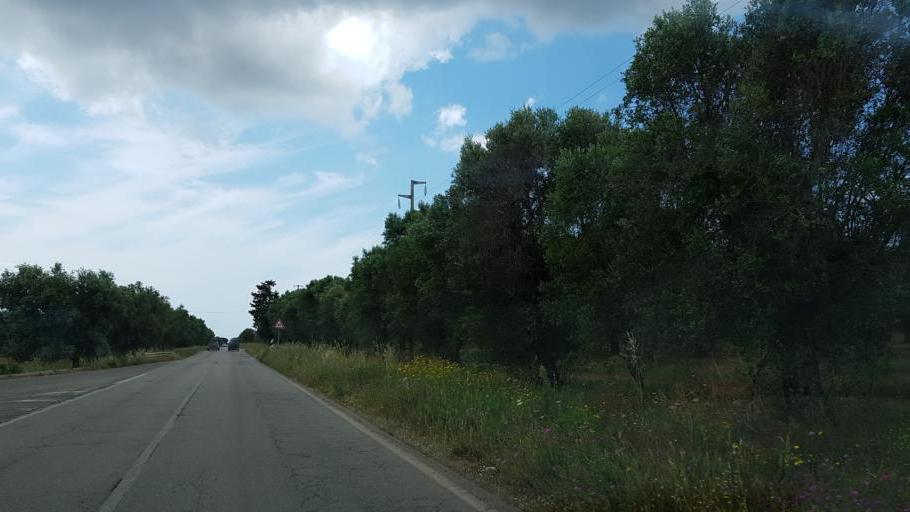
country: IT
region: Apulia
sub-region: Provincia di Brindisi
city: San Pancrazio Salentino
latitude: 40.3543
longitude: 17.8446
